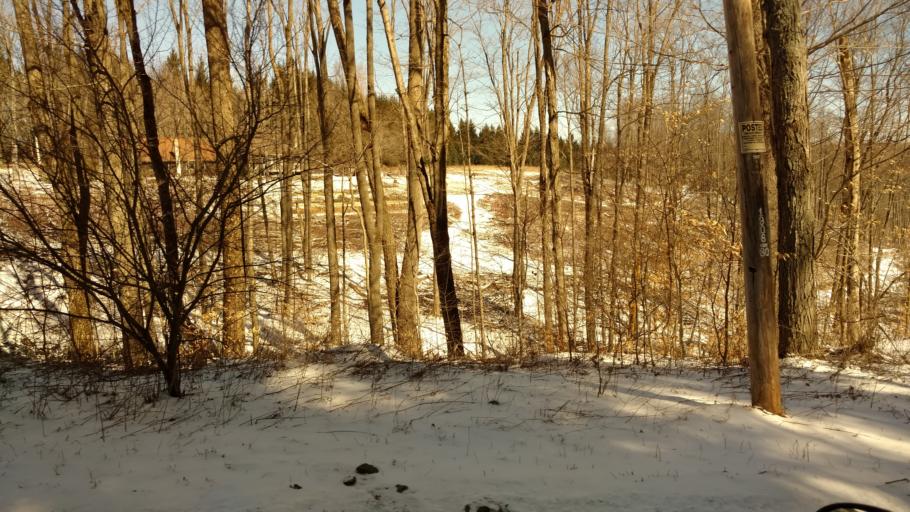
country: US
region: New York
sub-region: Allegany County
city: Wellsville
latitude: 42.0524
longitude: -78.0089
